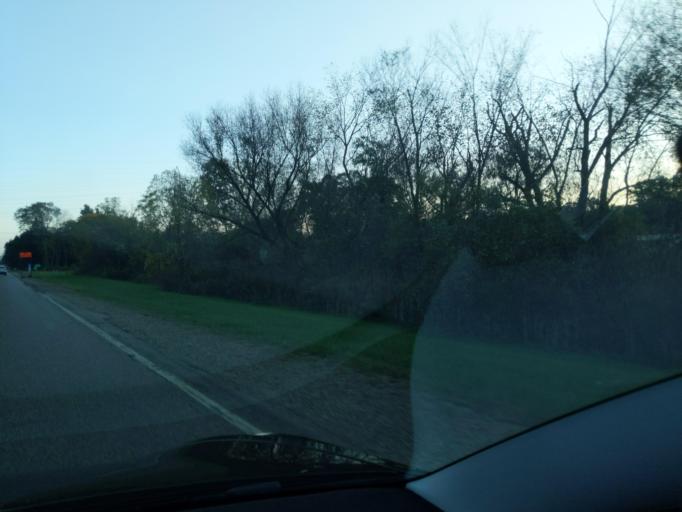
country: US
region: Michigan
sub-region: Jackson County
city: Jackson
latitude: 42.2706
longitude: -84.3844
